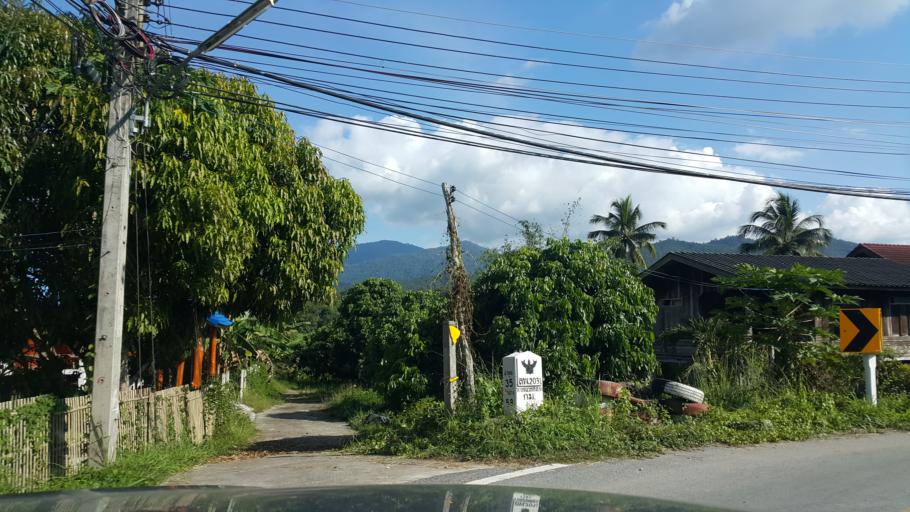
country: TH
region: Lamphun
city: Mae Tha
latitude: 18.5264
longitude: 99.2338
